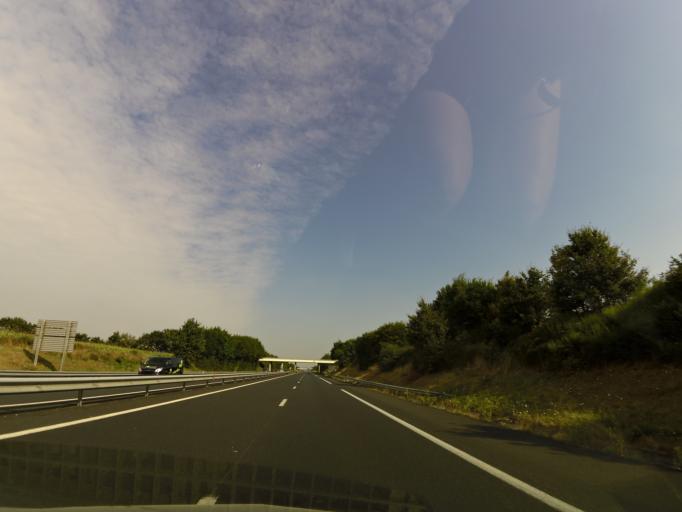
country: FR
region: Pays de la Loire
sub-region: Departement de la Vendee
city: Bouffere
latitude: 46.9487
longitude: -1.3536
